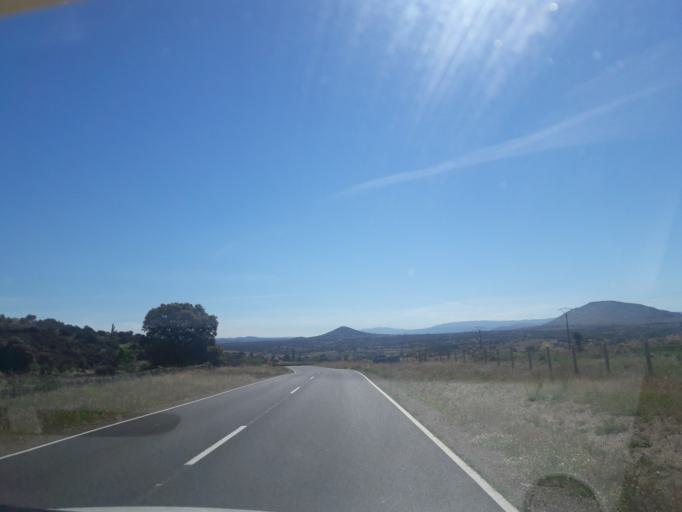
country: ES
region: Castille and Leon
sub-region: Provincia de Salamanca
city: Santibanez de Bejar
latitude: 40.4810
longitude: -5.6344
